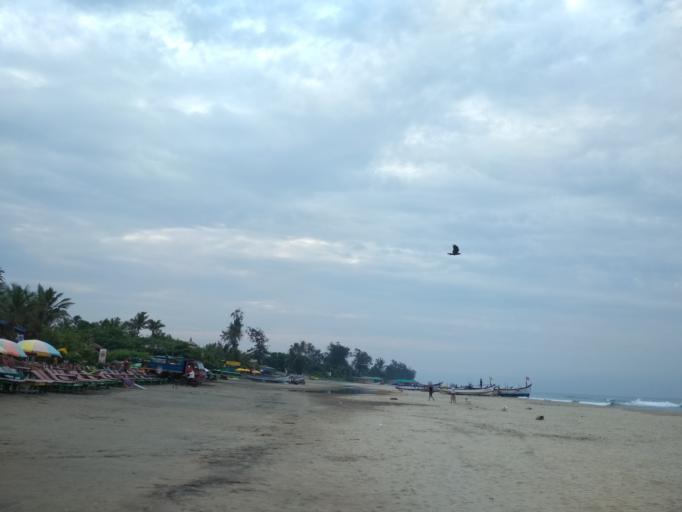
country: IN
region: Goa
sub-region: North Goa
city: Arambol
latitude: 15.6897
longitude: 73.7021
